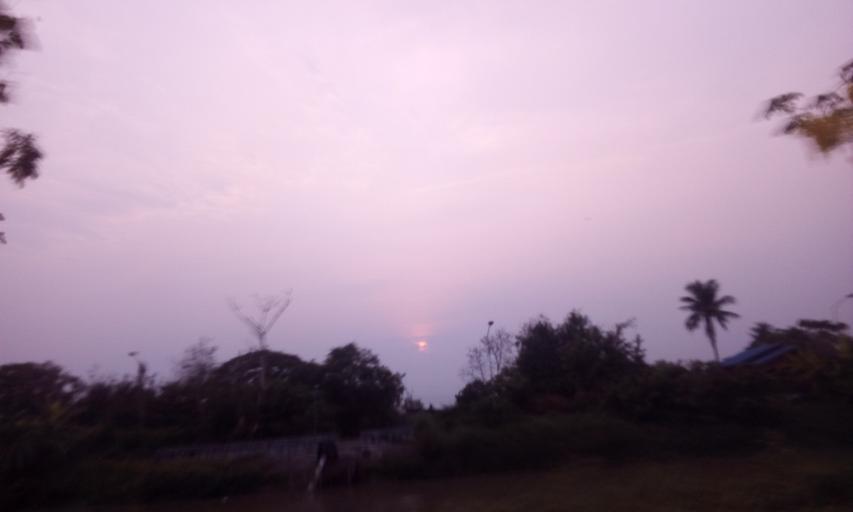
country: TH
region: Pathum Thani
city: Nong Suea
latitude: 14.0460
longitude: 100.8934
